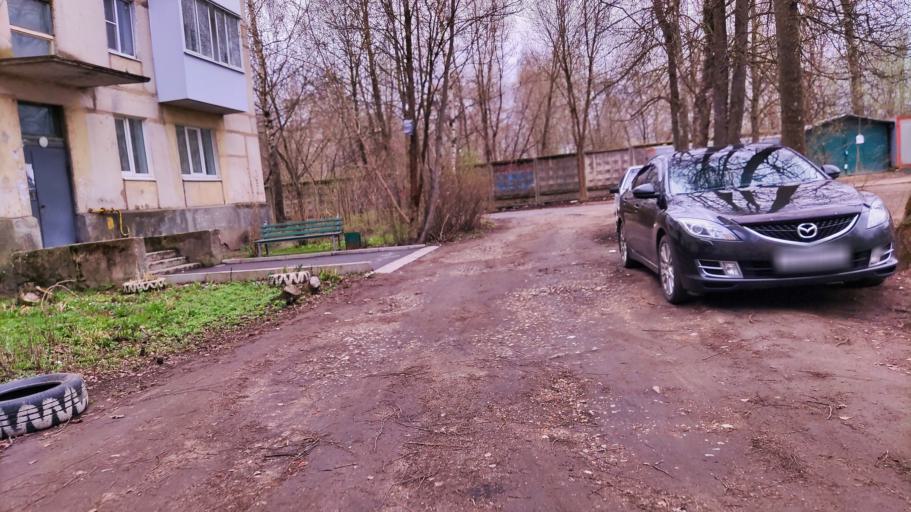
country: RU
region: Tverskaya
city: Rzhev
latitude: 56.2430
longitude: 34.3336
